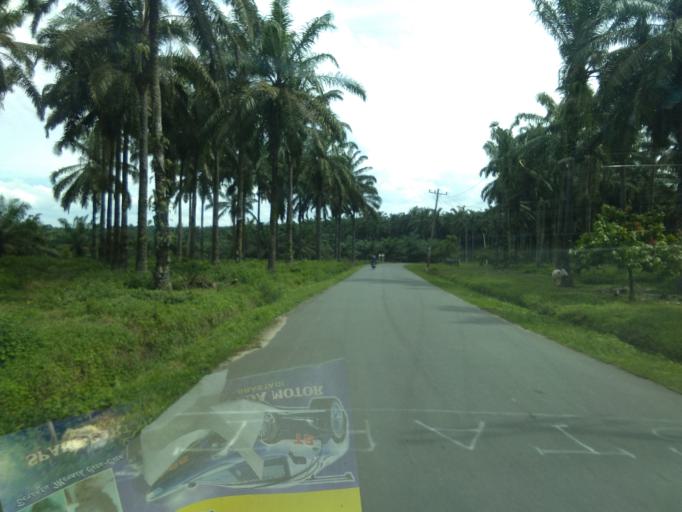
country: ID
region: North Sumatra
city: Deli Tua
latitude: 3.2948
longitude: 98.8072
